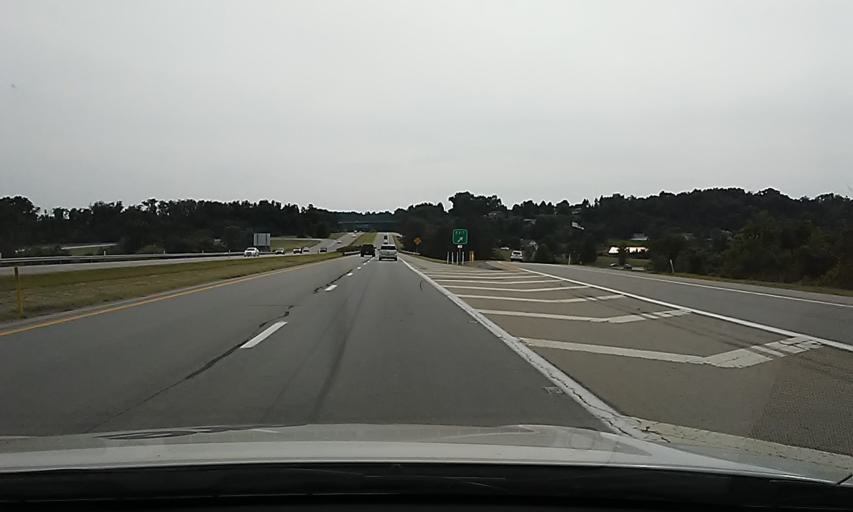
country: US
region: Pennsylvania
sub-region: Fayette County
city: South Uniontown
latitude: 39.9011
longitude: -79.7477
